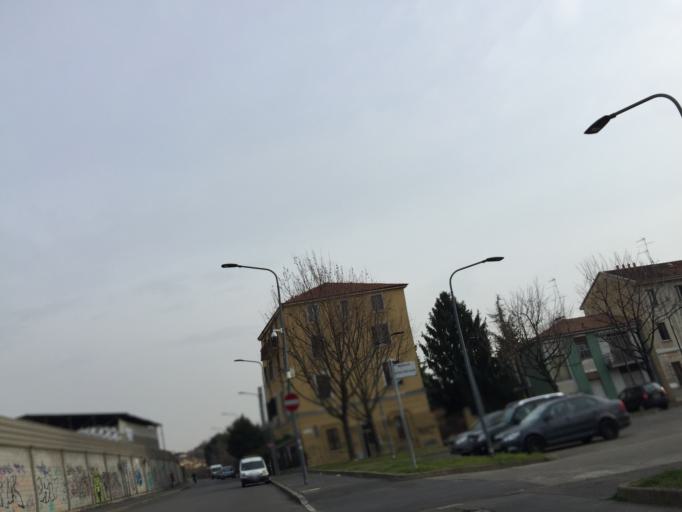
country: IT
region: Lombardy
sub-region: Citta metropolitana di Milano
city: Romano Banco
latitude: 45.4328
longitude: 9.1491
